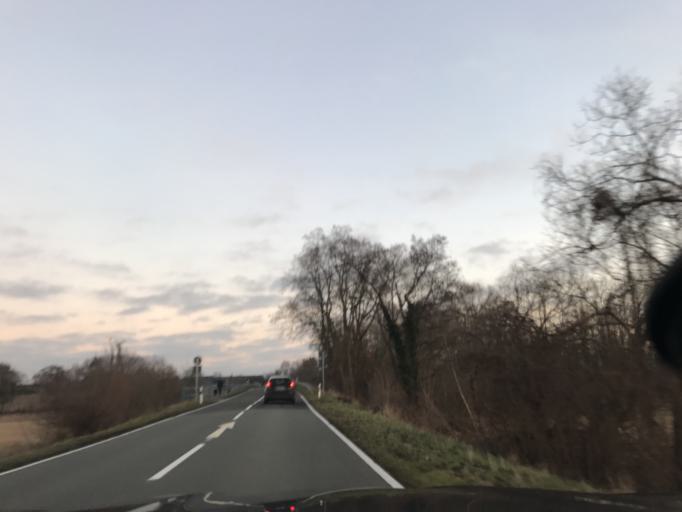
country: DE
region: Brandenburg
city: Pawesin
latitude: 52.5126
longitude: 12.7091
